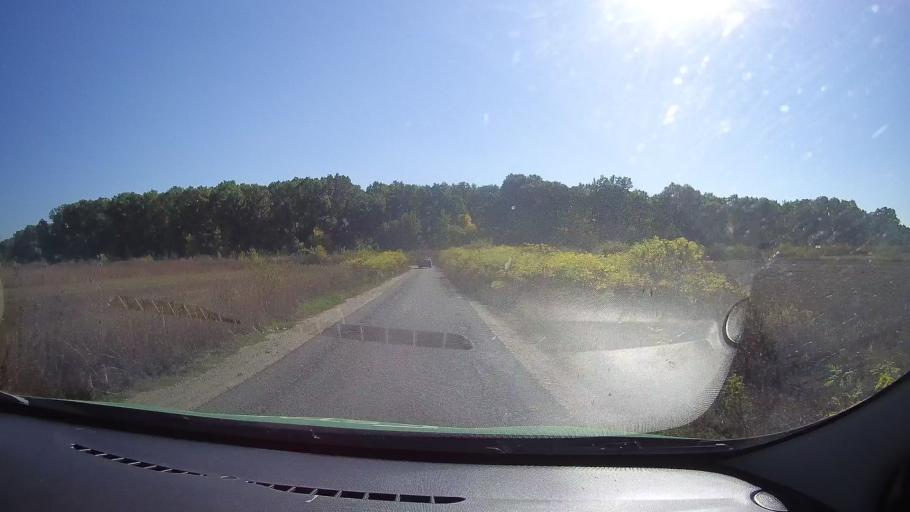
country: RO
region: Satu Mare
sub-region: Comuna Doba
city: Doba
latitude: 47.7186
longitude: 22.7283
